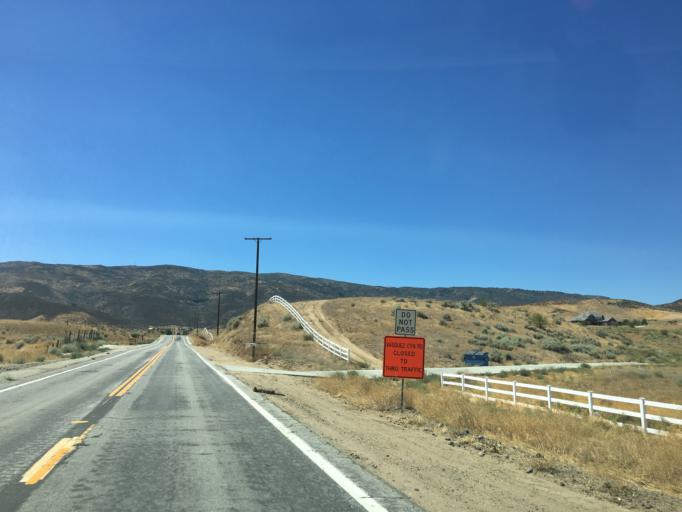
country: US
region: California
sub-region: Los Angeles County
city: Leona Valley
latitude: 34.6086
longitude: -118.2711
